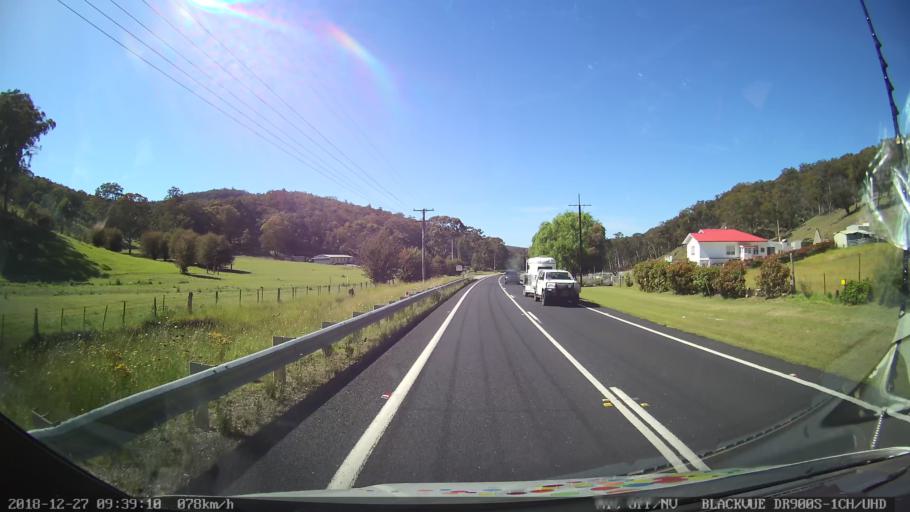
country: AU
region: New South Wales
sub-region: Lithgow
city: Portland
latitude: -33.2898
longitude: 150.0353
